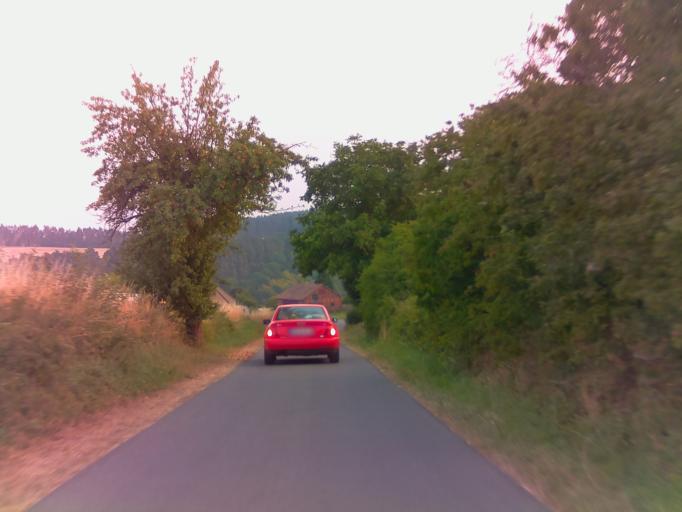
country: DE
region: Thuringia
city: Eichenberg
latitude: 50.7958
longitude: 11.5345
